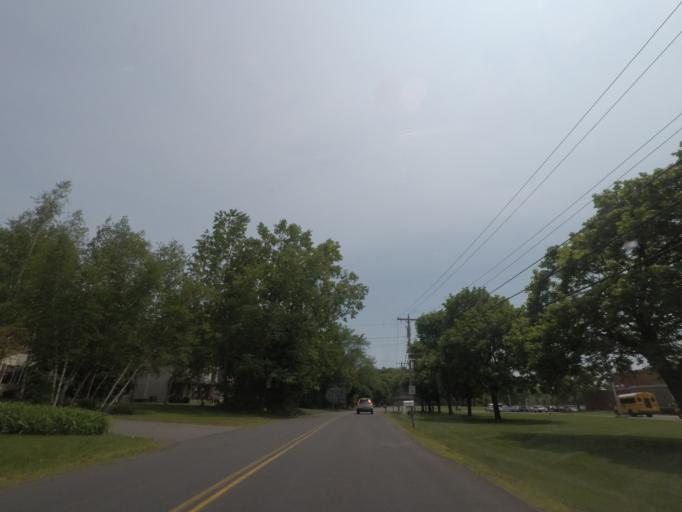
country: US
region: New York
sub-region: Rensselaer County
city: Castleton-on-Hudson
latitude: 42.5218
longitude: -73.7085
